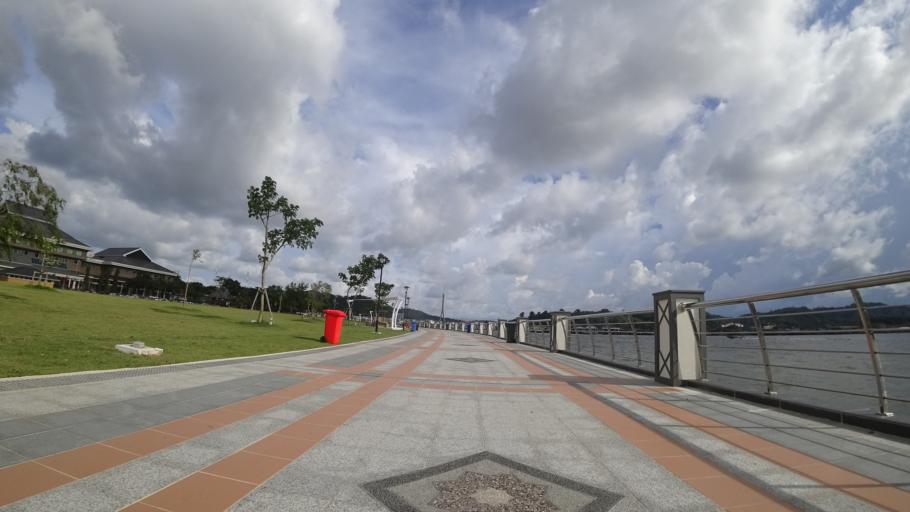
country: BN
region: Brunei and Muara
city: Bandar Seri Begawan
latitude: 4.8867
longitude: 114.9384
